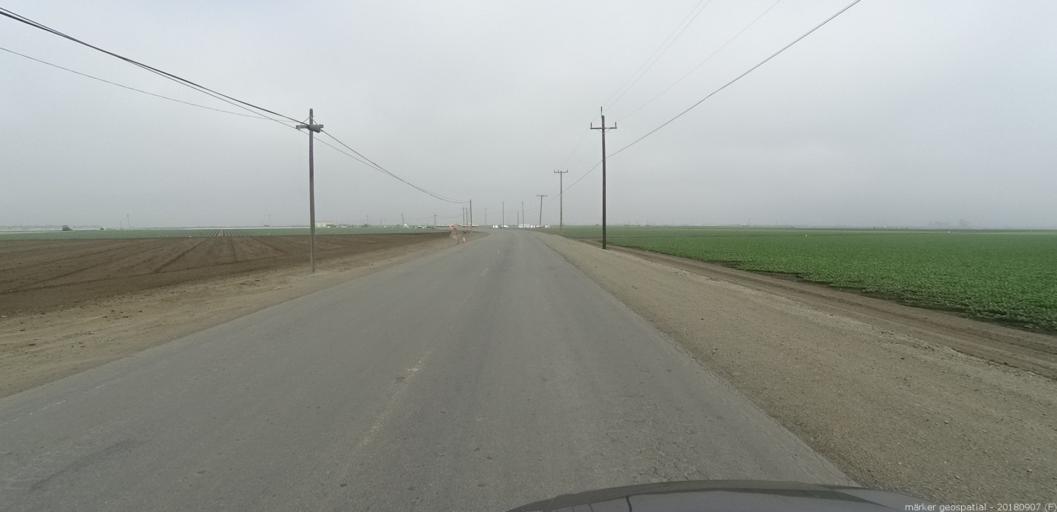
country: US
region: California
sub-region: Monterey County
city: Castroville
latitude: 36.7190
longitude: -121.7421
